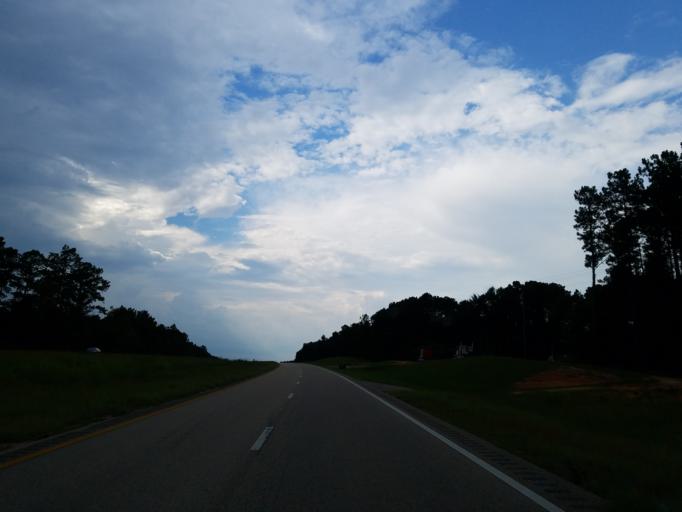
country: US
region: Mississippi
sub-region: Wayne County
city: Belmont
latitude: 31.4954
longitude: -88.4930
